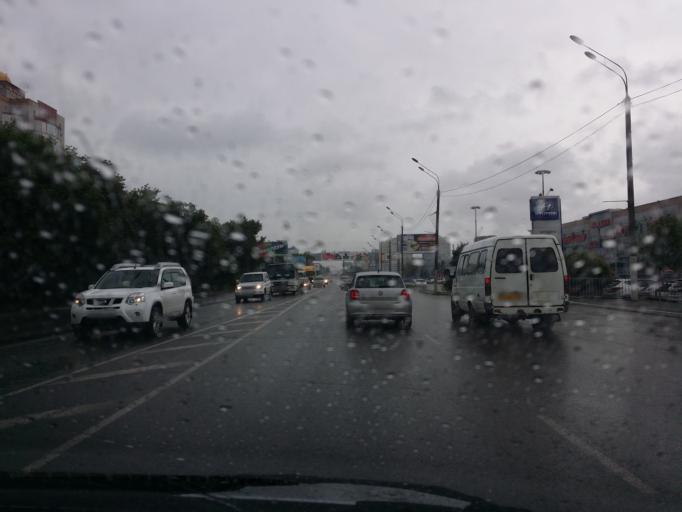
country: RU
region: Altai Krai
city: Novosilikatnyy
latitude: 53.3432
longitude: 83.6850
